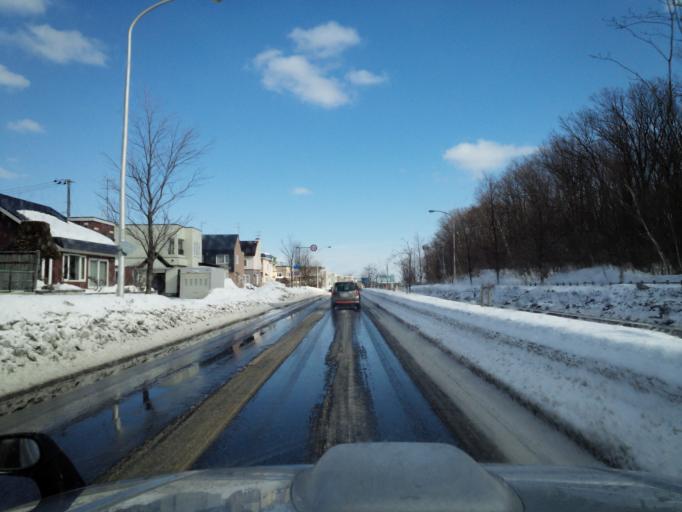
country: JP
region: Hokkaido
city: Kitahiroshima
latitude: 43.0052
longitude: 141.4606
